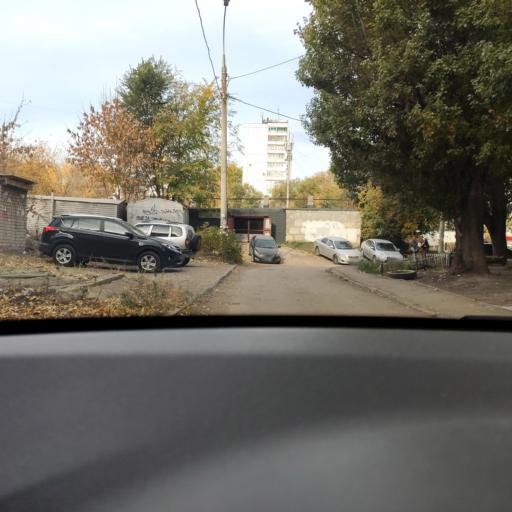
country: RU
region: Samara
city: Samara
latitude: 53.2473
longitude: 50.2567
